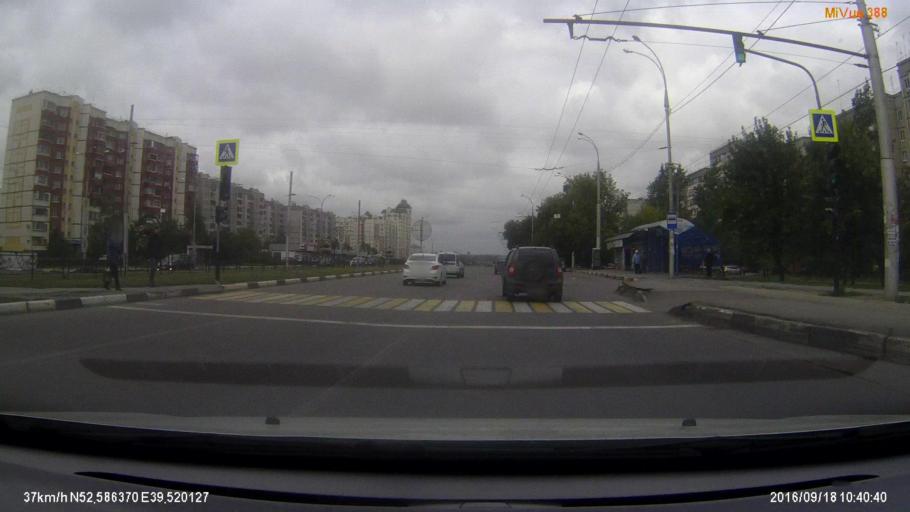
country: RU
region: Lipetsk
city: Syrskoye
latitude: 52.5858
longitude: 39.5205
